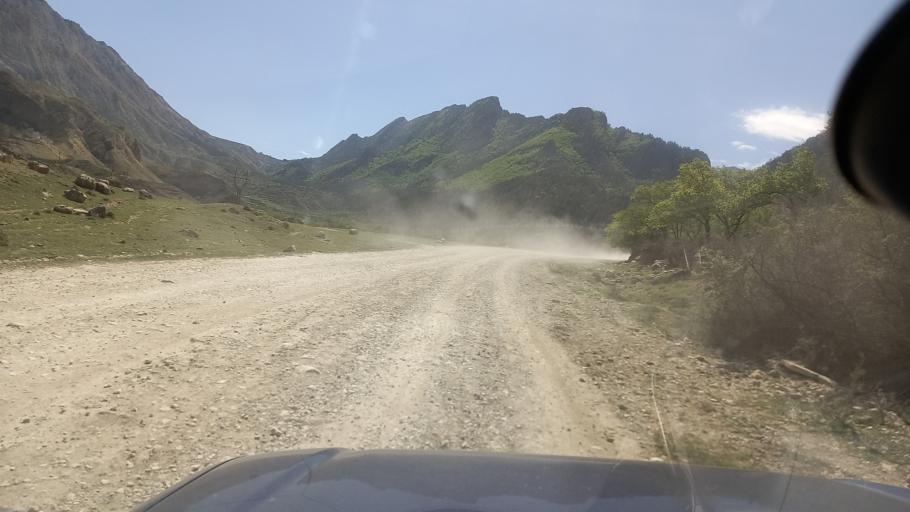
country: RU
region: Dagestan
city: Gunib
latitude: 42.4701
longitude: 46.8826
